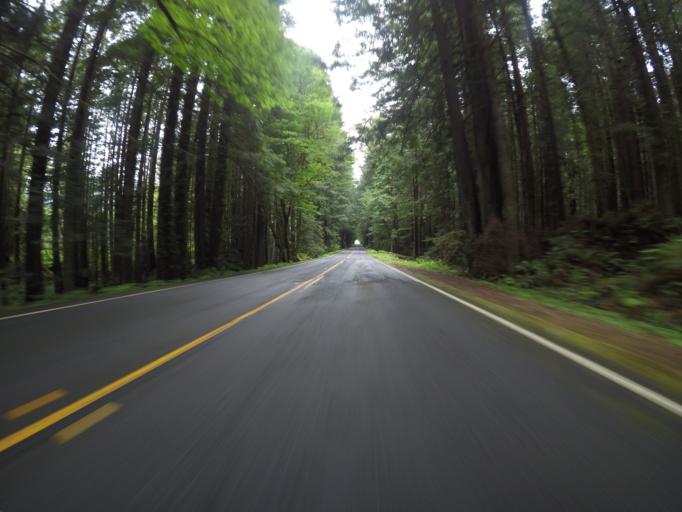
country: US
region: California
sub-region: Humboldt County
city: Rio Dell
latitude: 40.4463
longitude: -124.0090
